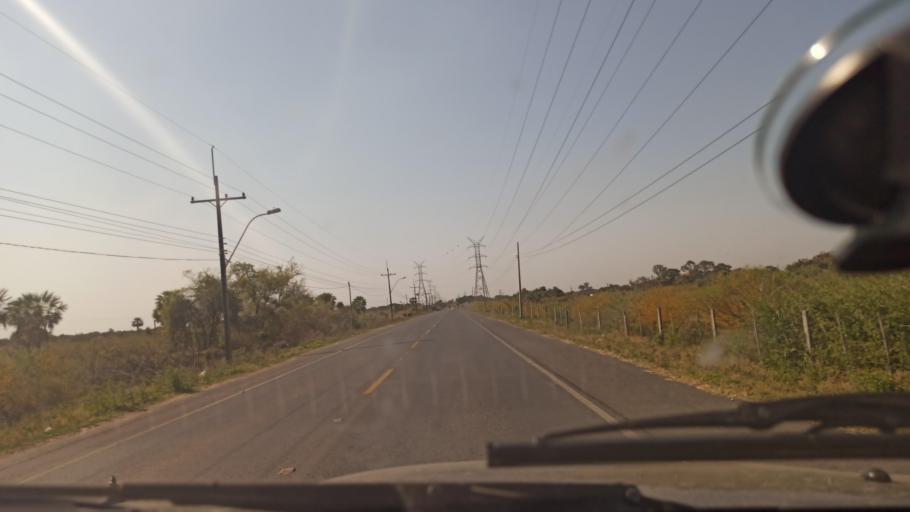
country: PY
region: Presidente Hayes
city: Nanawa
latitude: -25.2474
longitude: -57.6678
